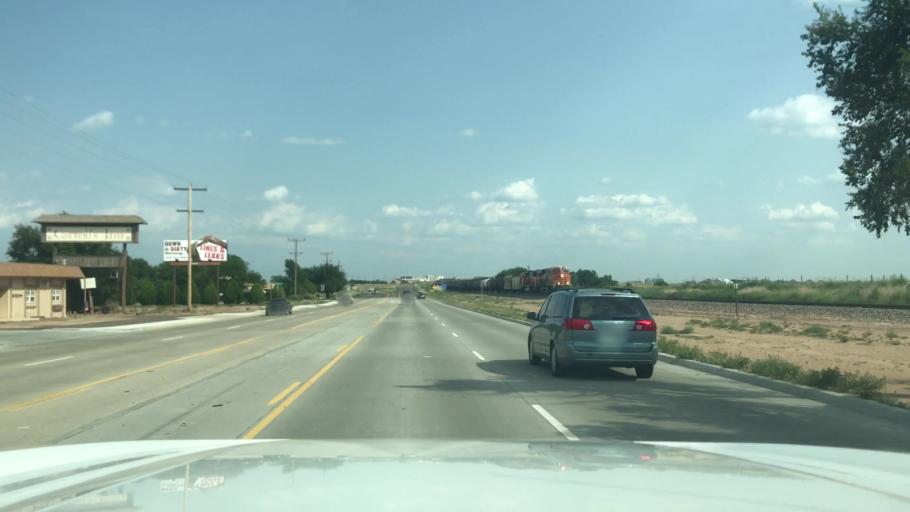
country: US
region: Texas
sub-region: Dallam County
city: Dalhart
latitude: 36.0489
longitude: -102.4978
